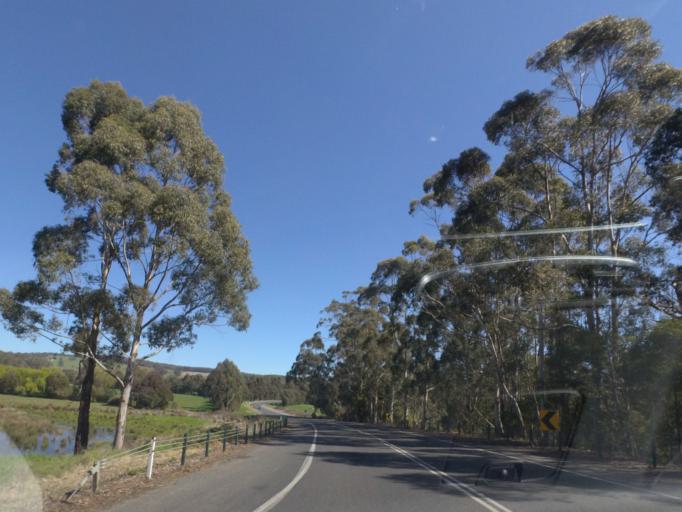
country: AU
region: Victoria
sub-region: Latrobe
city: Morwell
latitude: -38.3810
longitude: 146.2861
